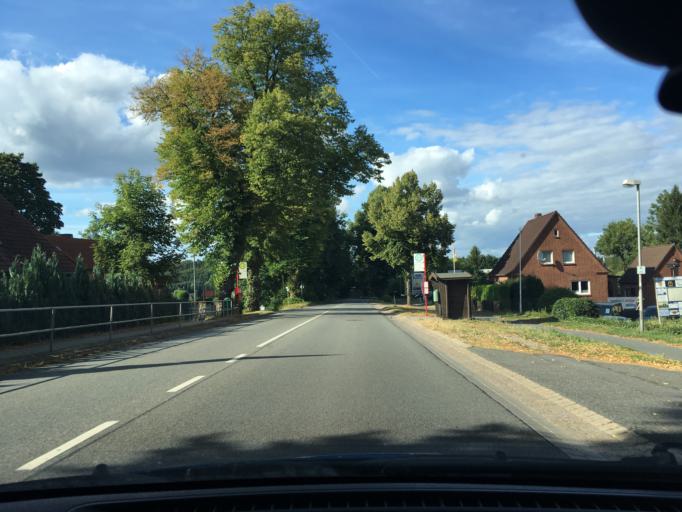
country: DE
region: Lower Saxony
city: Seevetal
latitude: 53.4053
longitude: 9.9251
